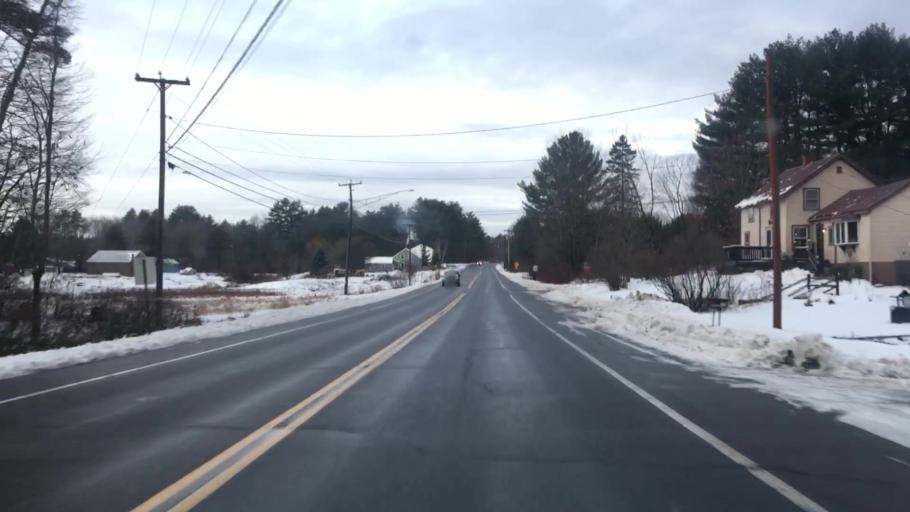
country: US
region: Maine
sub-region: York County
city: Limington
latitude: 43.7336
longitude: -70.6544
